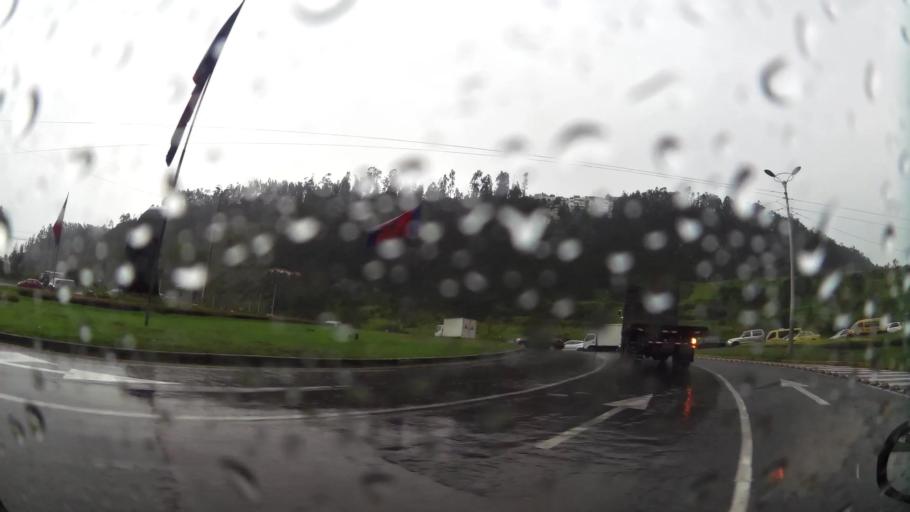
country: EC
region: Pichincha
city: Quito
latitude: -0.1501
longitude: -78.4527
